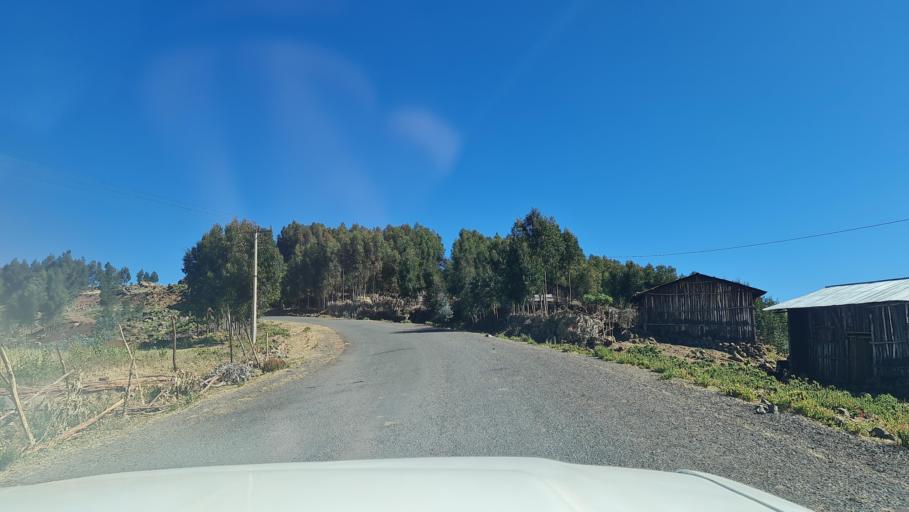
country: ET
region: Amhara
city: Debark'
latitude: 13.1086
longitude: 38.1488
